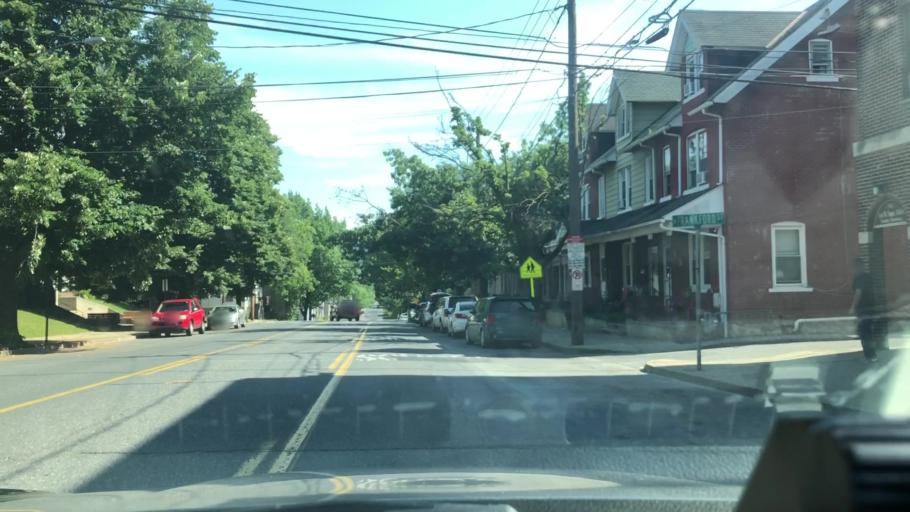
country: US
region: Pennsylvania
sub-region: Northampton County
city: Bethlehem
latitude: 40.6286
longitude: -75.3817
